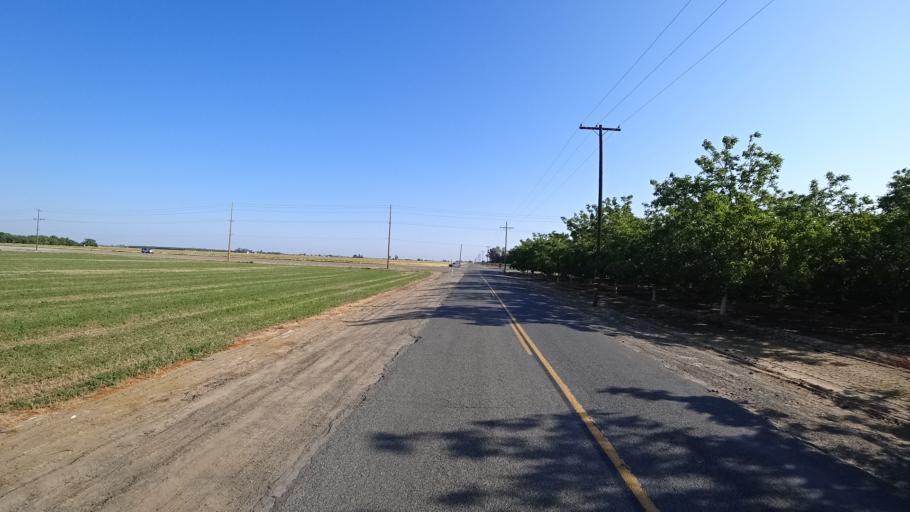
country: US
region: California
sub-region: Kings County
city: Home Garden
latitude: 36.2977
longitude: -119.5652
